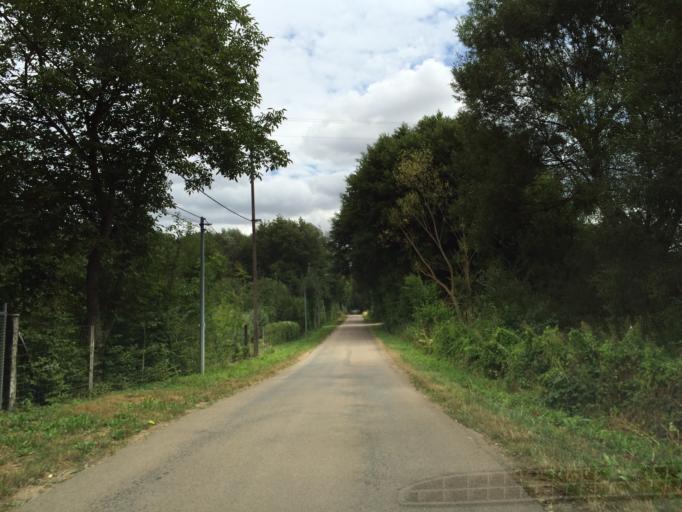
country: FR
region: Bourgogne
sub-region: Departement de l'Yonne
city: Aillant-sur-Tholon
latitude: 47.8638
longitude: 3.3943
